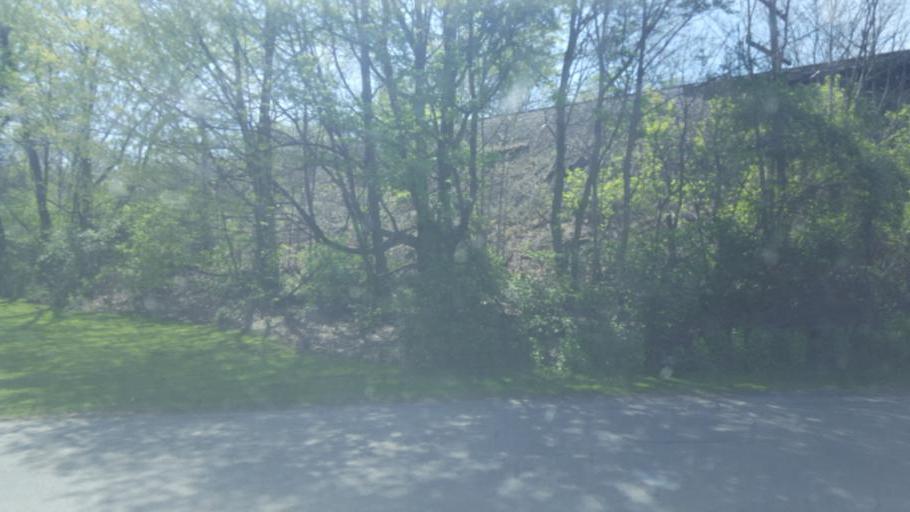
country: US
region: Ohio
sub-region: Medina County
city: Lodi
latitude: 41.0300
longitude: -82.0142
